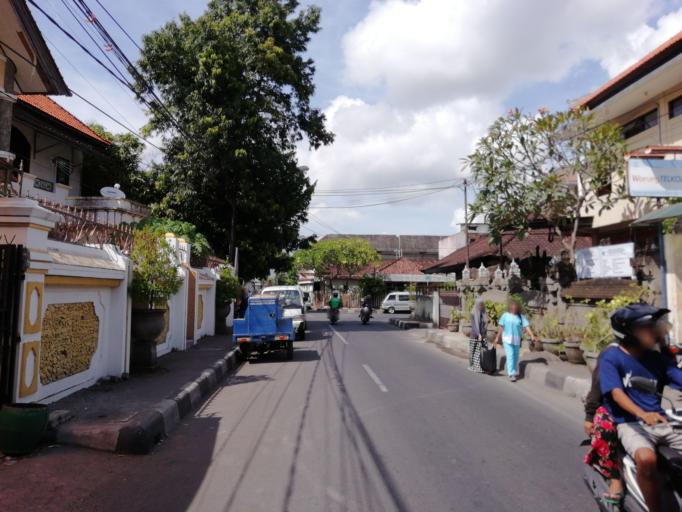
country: ID
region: Bali
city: Denpasar
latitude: -8.6746
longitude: 115.2162
